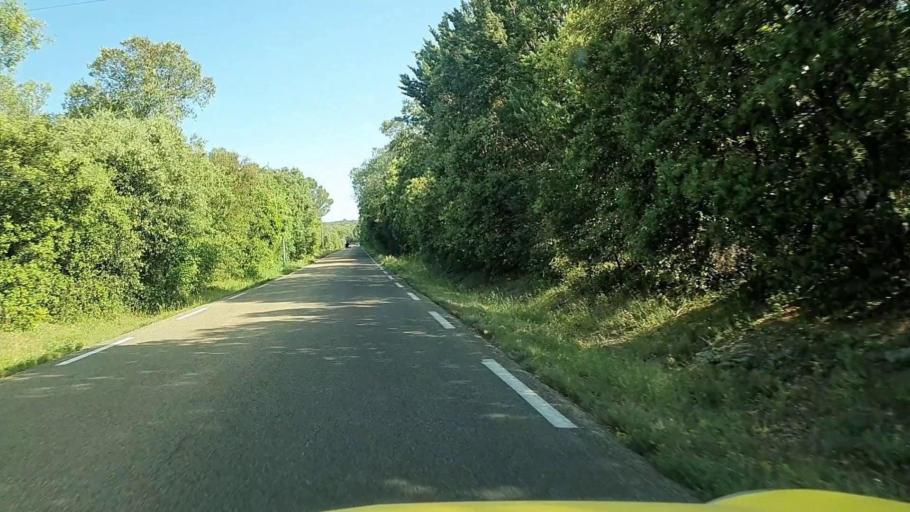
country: FR
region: Languedoc-Roussillon
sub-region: Departement du Gard
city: Montaren-et-Saint-Mediers
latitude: 44.0530
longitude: 4.4023
